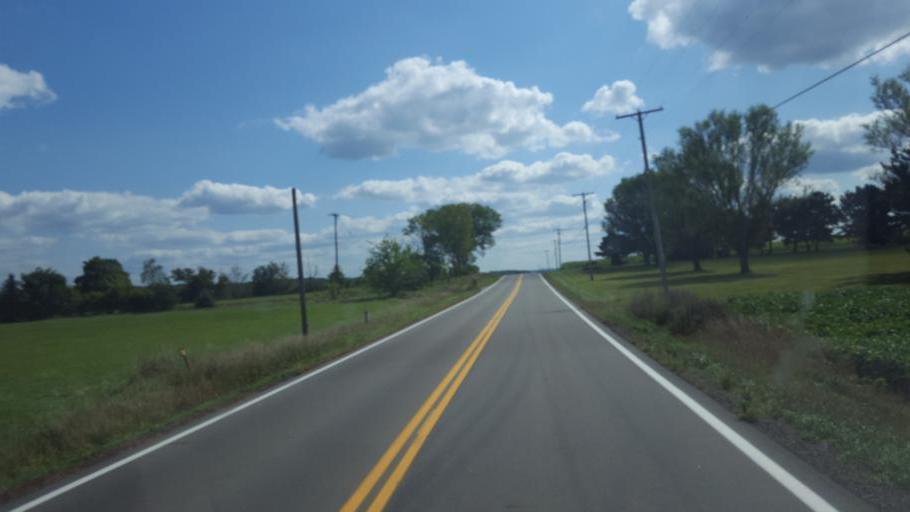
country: US
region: Ohio
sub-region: Ashland County
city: Ashland
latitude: 40.8654
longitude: -82.2120
